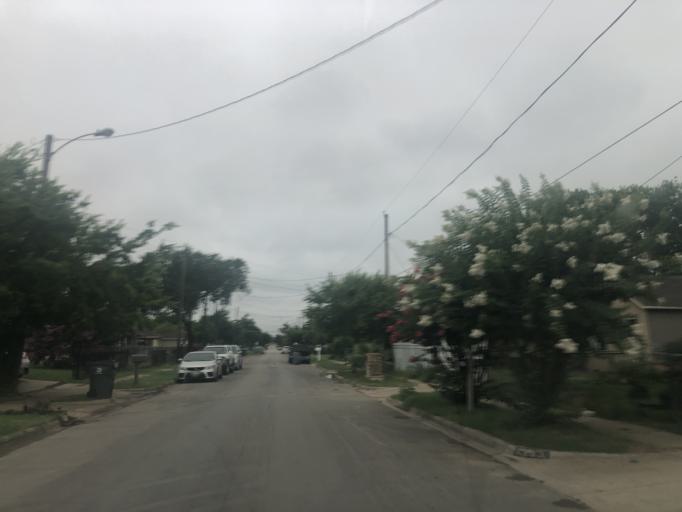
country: US
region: Texas
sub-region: Dallas County
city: Cockrell Hill
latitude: 32.7807
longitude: -96.8751
